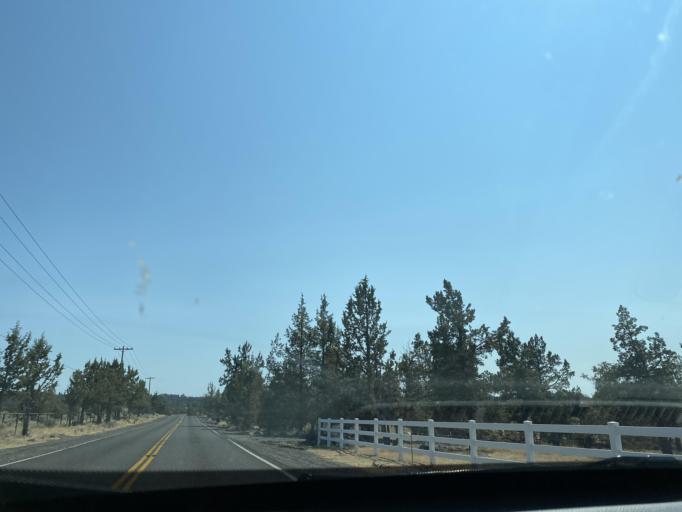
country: US
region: Oregon
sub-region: Deschutes County
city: Terrebonne
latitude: 44.3604
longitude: -121.1586
